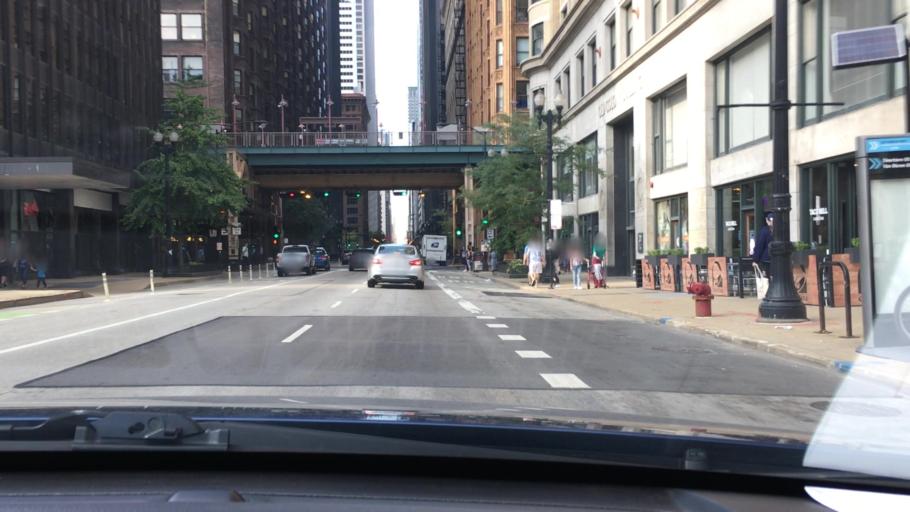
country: US
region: Illinois
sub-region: Cook County
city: Chicago
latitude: 41.8763
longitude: -87.6292
